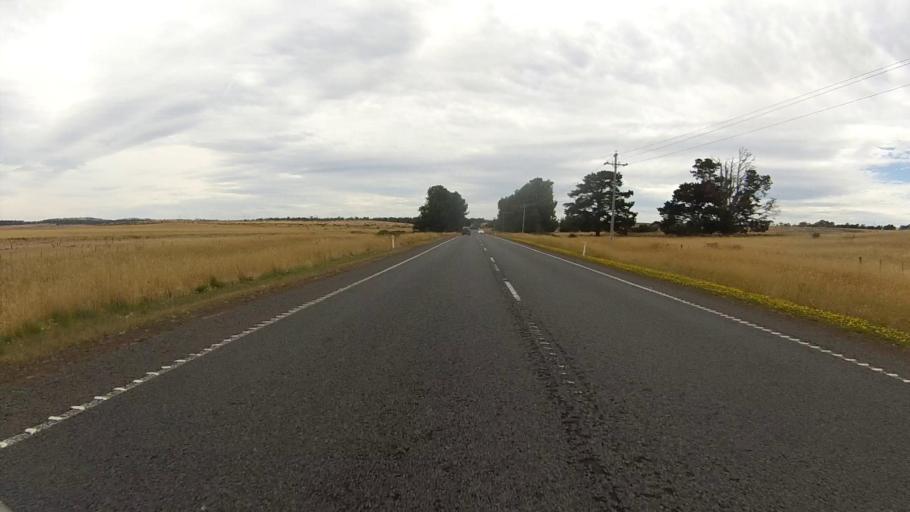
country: AU
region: Tasmania
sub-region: Northern Midlands
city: Evandale
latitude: -41.8510
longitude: 147.4512
